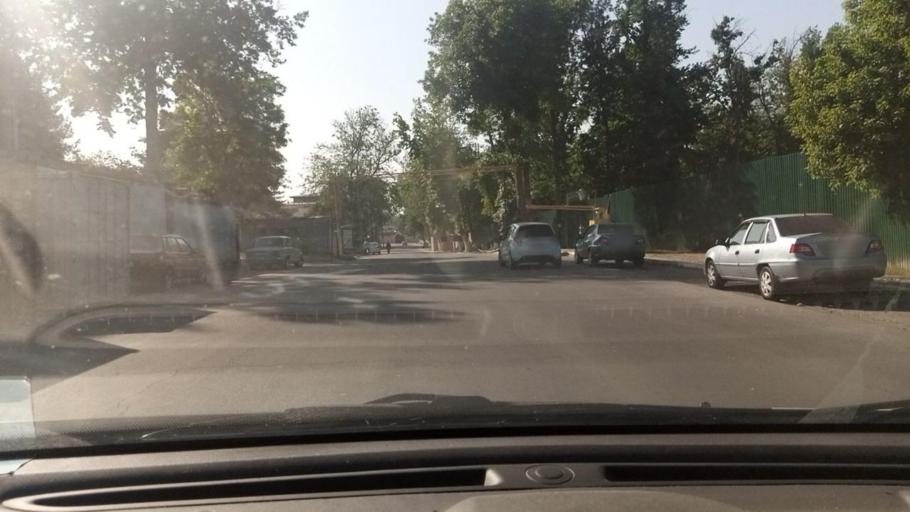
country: UZ
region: Toshkent
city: Salor
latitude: 41.3364
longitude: 69.3574
